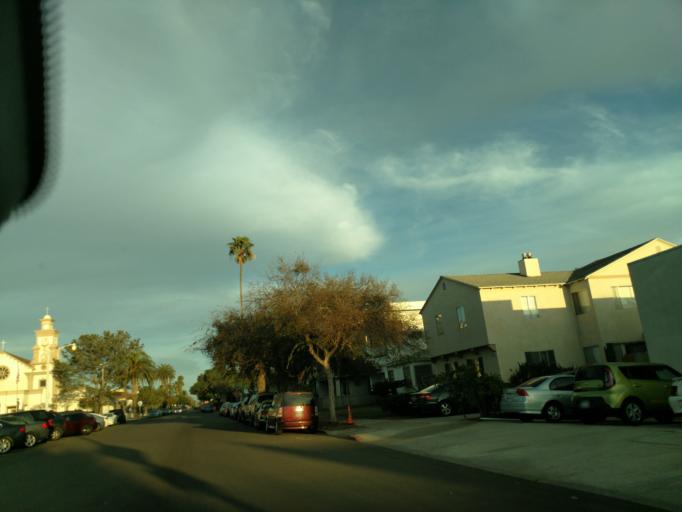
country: US
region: California
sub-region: San Diego County
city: La Jolla
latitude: 32.8000
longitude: -117.2537
